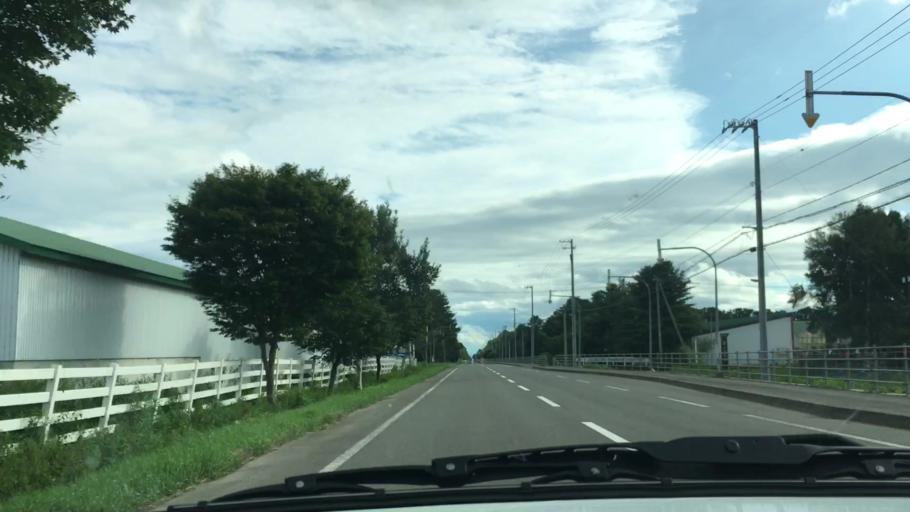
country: JP
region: Hokkaido
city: Otofuke
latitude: 43.2505
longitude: 143.2991
